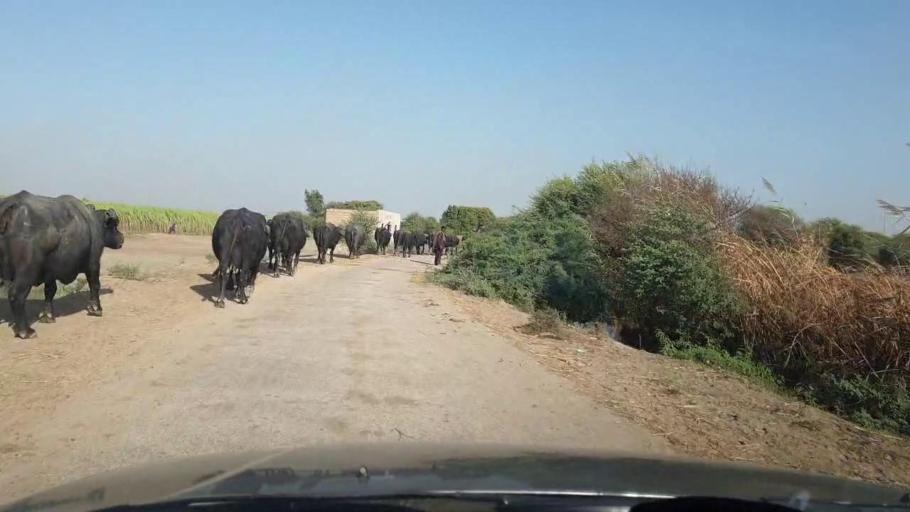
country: PK
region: Sindh
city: Bulri
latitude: 25.1106
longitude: 68.2662
